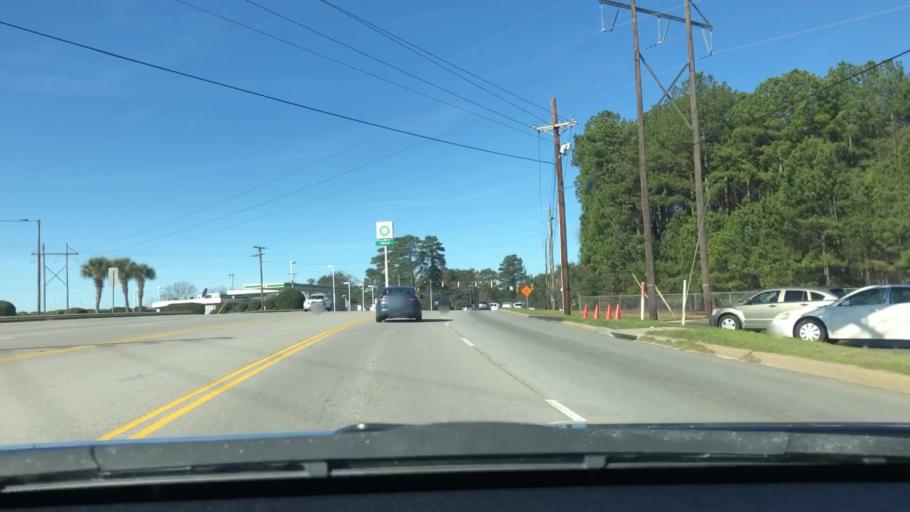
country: US
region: South Carolina
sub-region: Lexington County
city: Oak Grove
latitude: 34.0081
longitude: -81.1444
